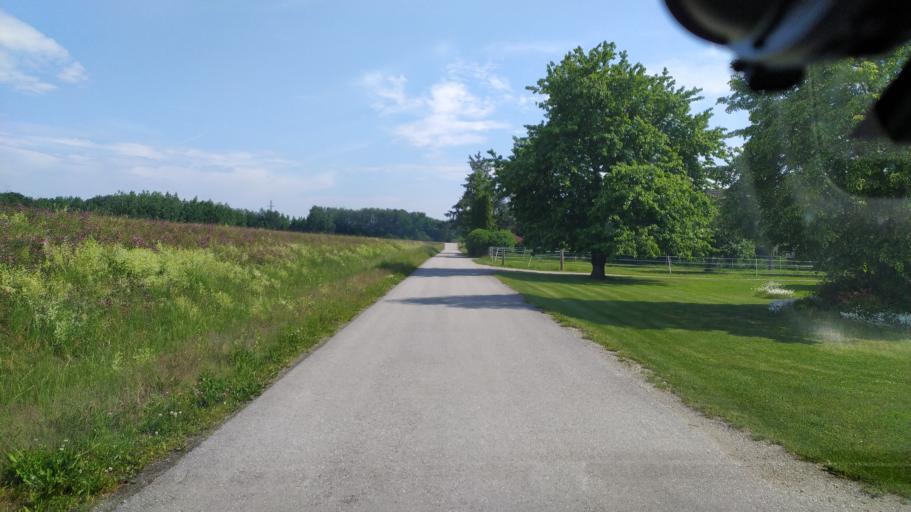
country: AT
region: Lower Austria
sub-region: Politischer Bezirk Amstetten
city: Strengberg
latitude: 48.1782
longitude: 14.6784
